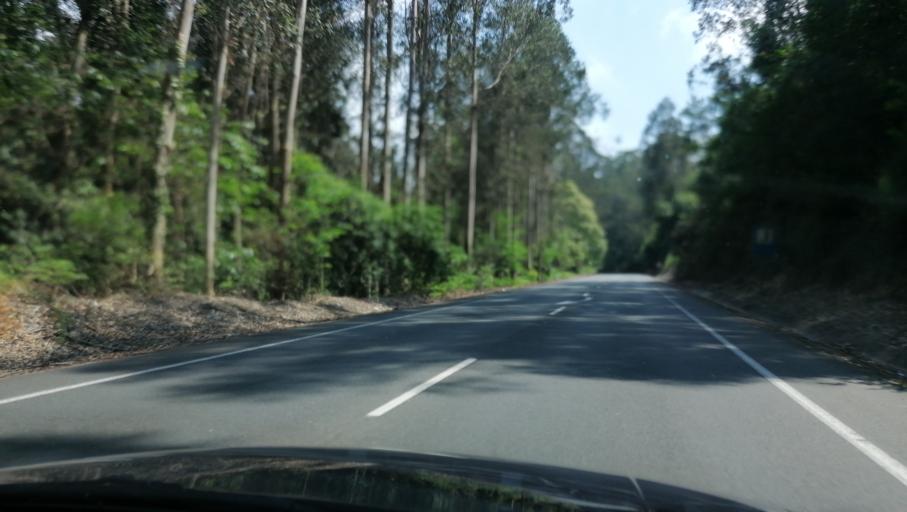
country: ES
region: Galicia
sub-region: Provincia de Pontevedra
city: Gondomar
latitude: 42.0813
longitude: -8.7505
